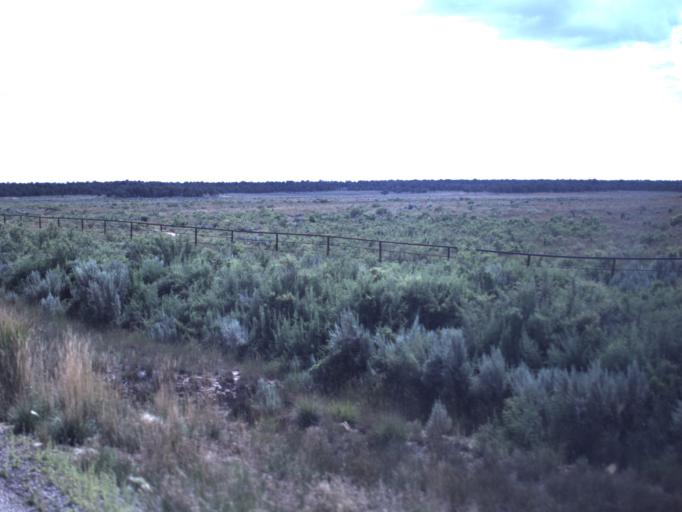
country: US
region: Utah
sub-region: Duchesne County
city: Duchesne
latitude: 40.2723
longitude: -110.7029
